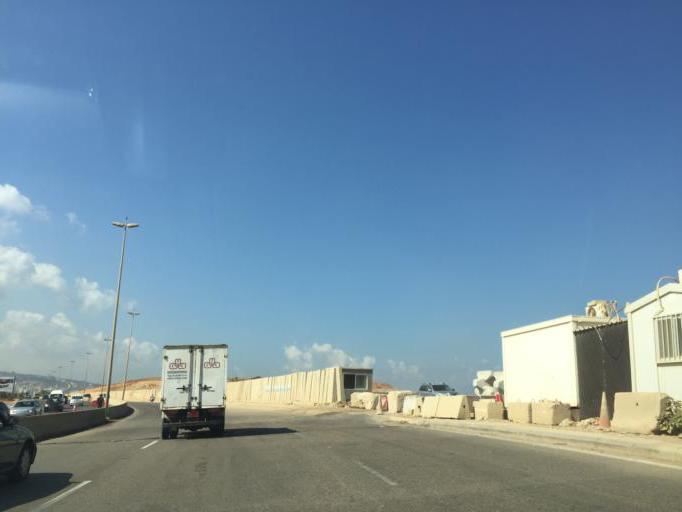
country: LB
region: Mont-Liban
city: Baabda
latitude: 33.8170
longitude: 35.4832
